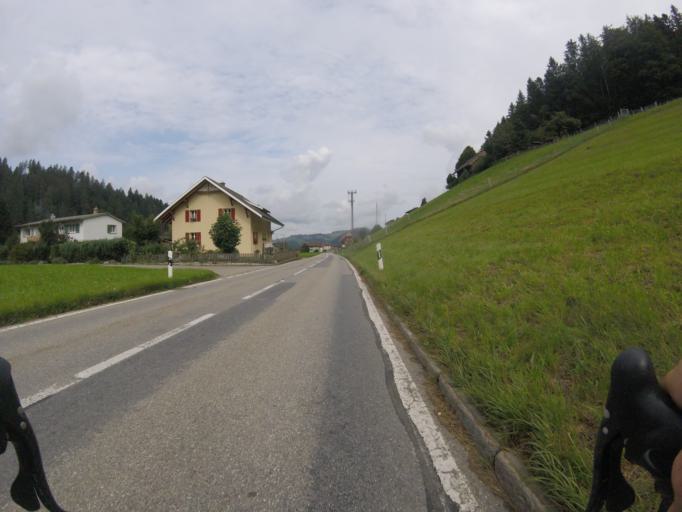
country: CH
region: Bern
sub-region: Emmental District
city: Lutzelfluh
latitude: 46.9963
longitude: 7.6818
